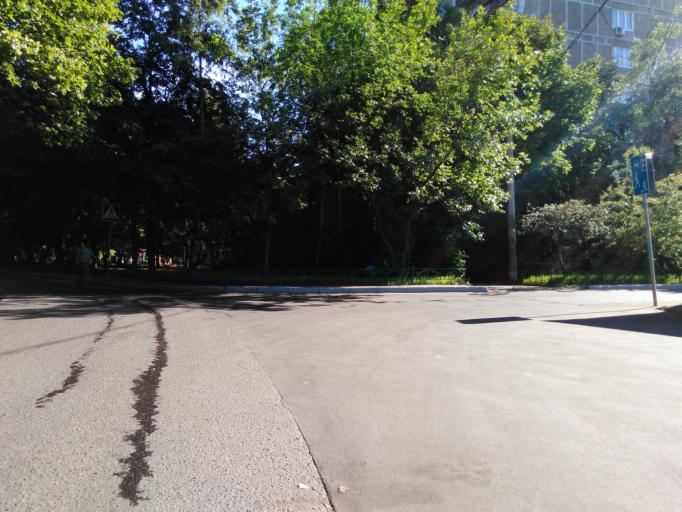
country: RU
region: Moscow
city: Troparevo
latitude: 55.6622
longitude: 37.4932
